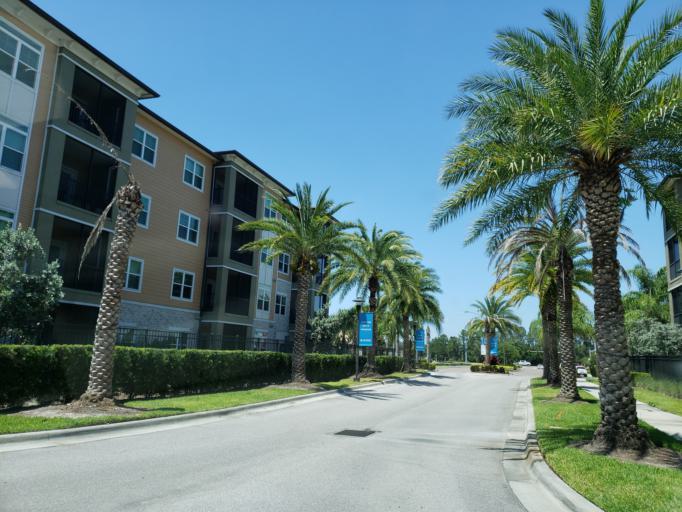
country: US
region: Florida
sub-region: Hillsborough County
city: Progress Village
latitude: 27.9256
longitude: -82.3357
